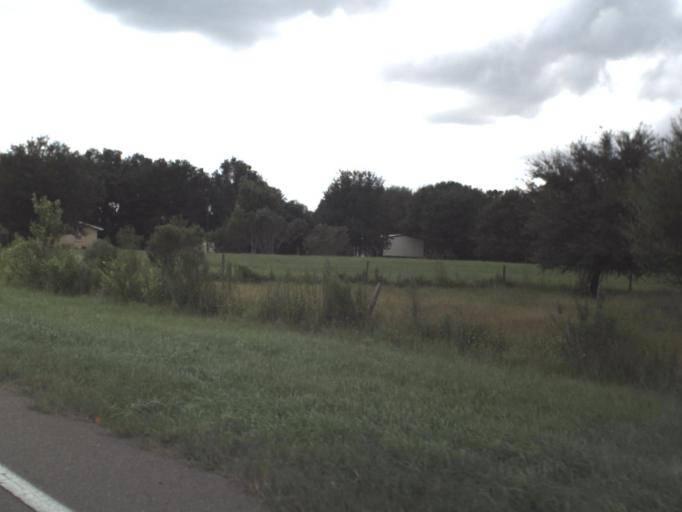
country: US
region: Florida
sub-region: Hardee County
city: Zolfo Springs
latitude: 27.4976
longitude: -81.8239
